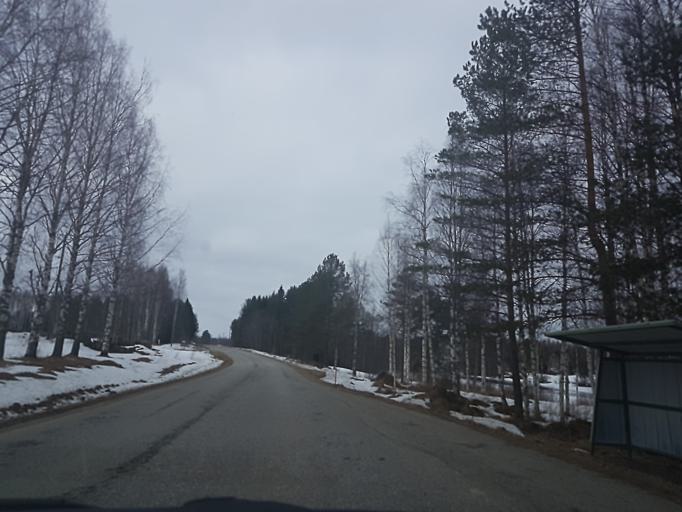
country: FI
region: Northern Savo
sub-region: Koillis-Savo
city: Kaavi
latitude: 62.9953
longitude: 28.7192
